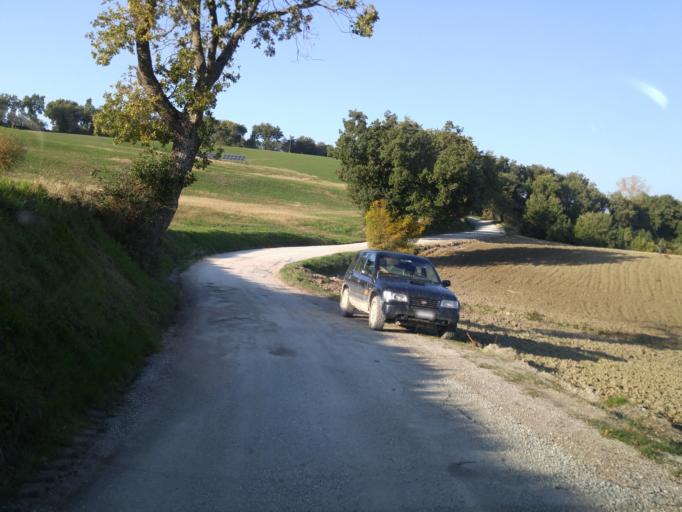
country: IT
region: The Marches
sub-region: Provincia di Pesaro e Urbino
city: Fossombrone
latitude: 43.7099
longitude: 12.8151
